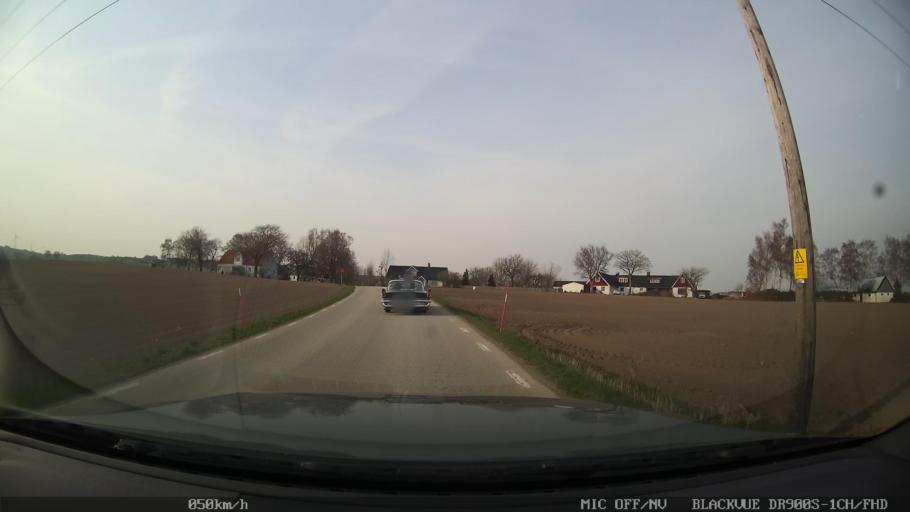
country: SE
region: Skane
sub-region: Ystads Kommun
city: Ystad
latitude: 55.4624
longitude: 13.8242
